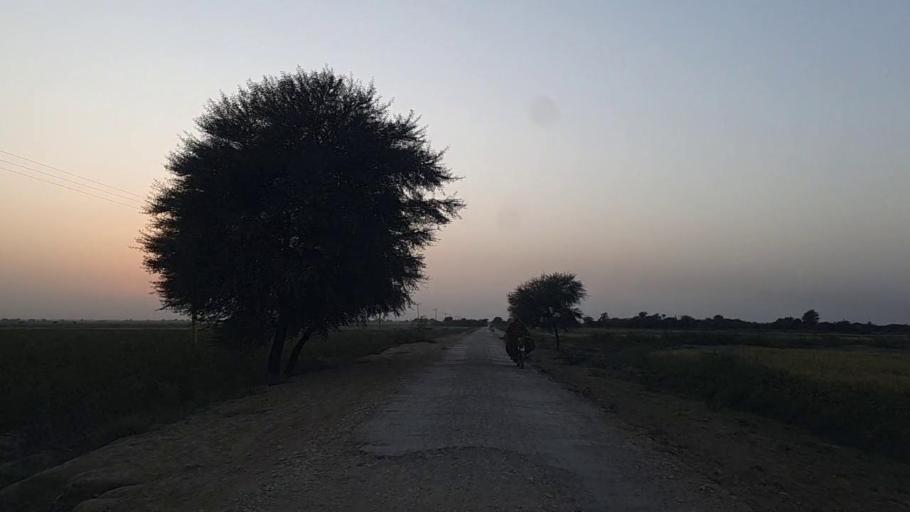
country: PK
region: Sindh
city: Naukot
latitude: 24.7501
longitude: 69.3074
